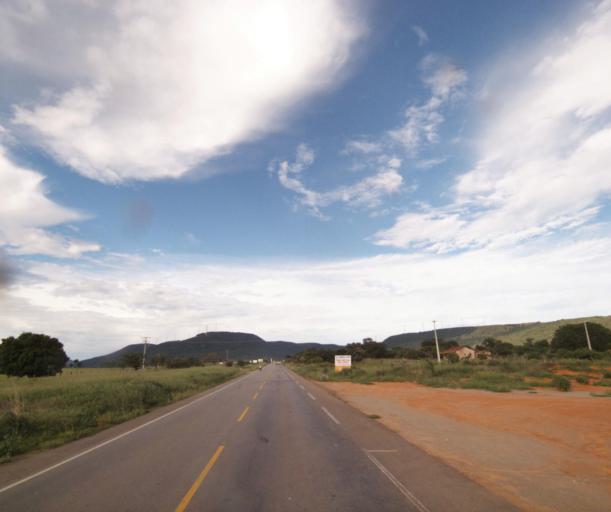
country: BR
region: Bahia
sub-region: Guanambi
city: Guanambi
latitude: -14.1735
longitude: -42.7279
